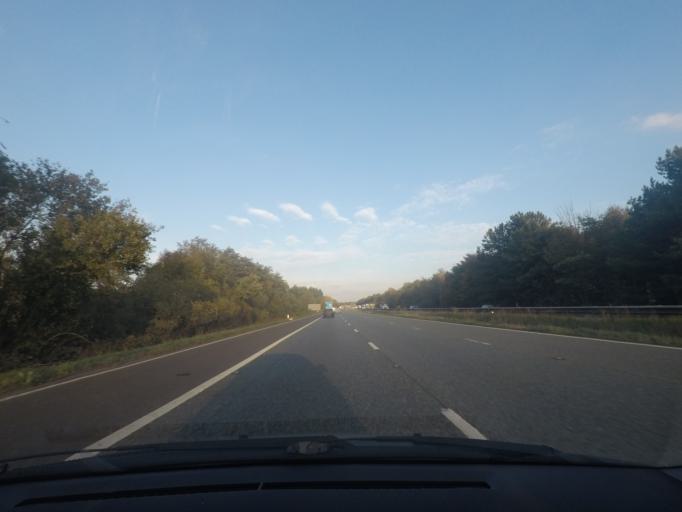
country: GB
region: England
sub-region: North Lincolnshire
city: Worlaby
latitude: 53.5792
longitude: -0.4506
